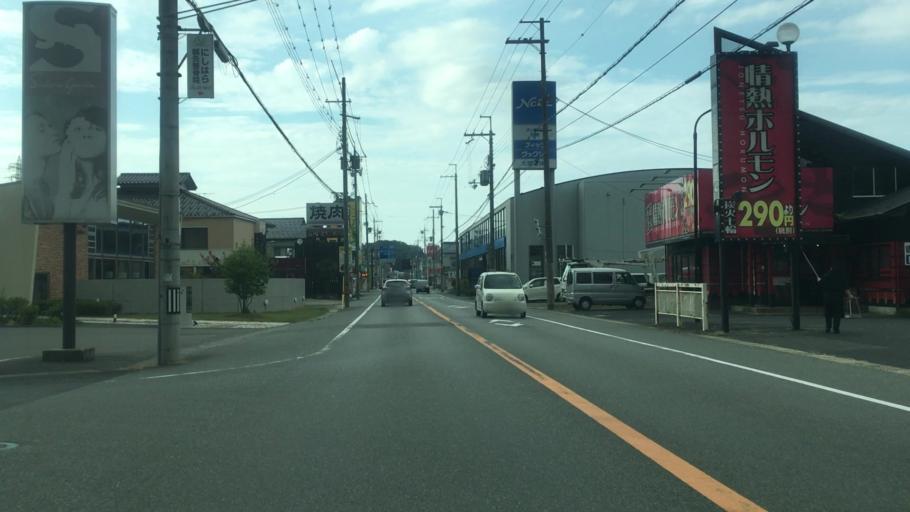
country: JP
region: Hyogo
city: Toyooka
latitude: 35.5261
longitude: 134.8210
